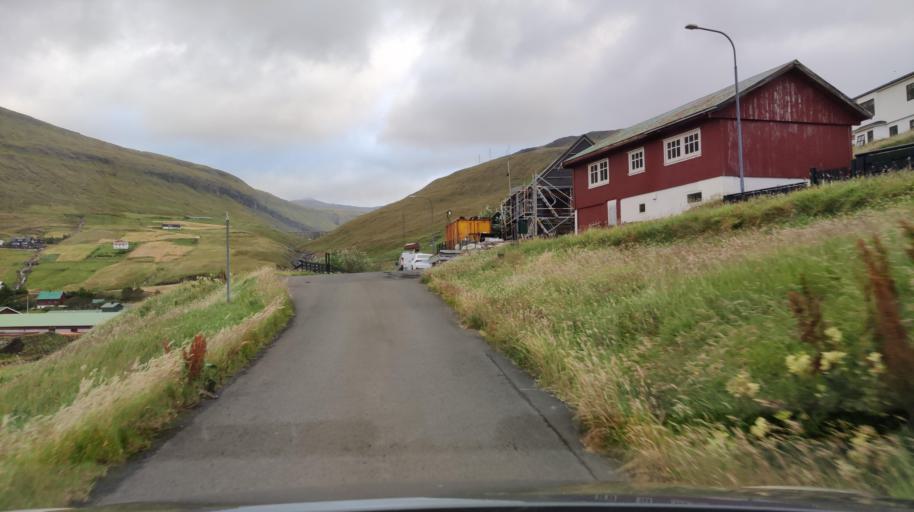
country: FO
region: Streymoy
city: Vestmanna
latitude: 62.1501
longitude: -7.1527
